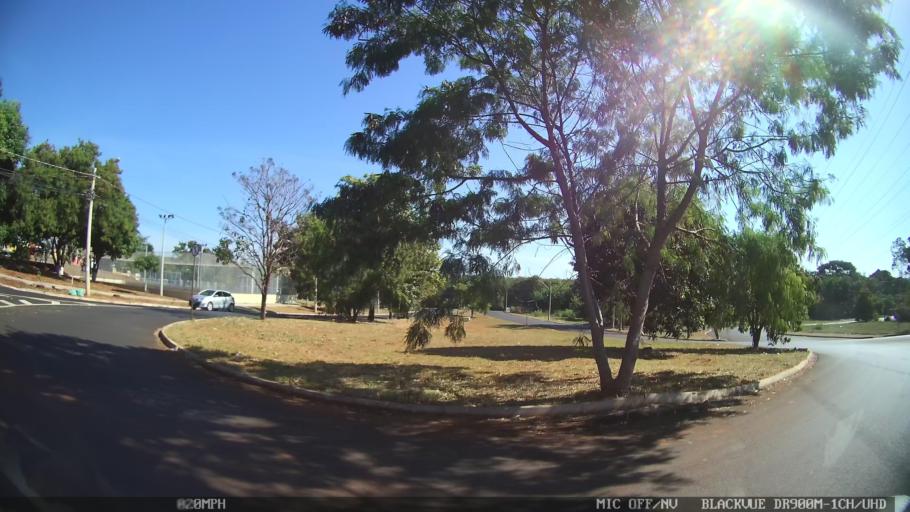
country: BR
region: Sao Paulo
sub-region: Ribeirao Preto
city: Ribeirao Preto
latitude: -21.2238
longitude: -47.7663
